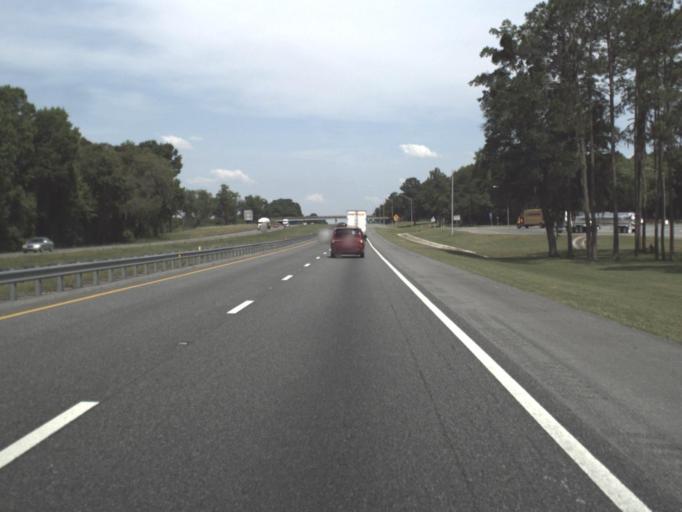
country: US
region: Florida
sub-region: Suwannee County
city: Wellborn
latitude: 30.2750
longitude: -82.8016
